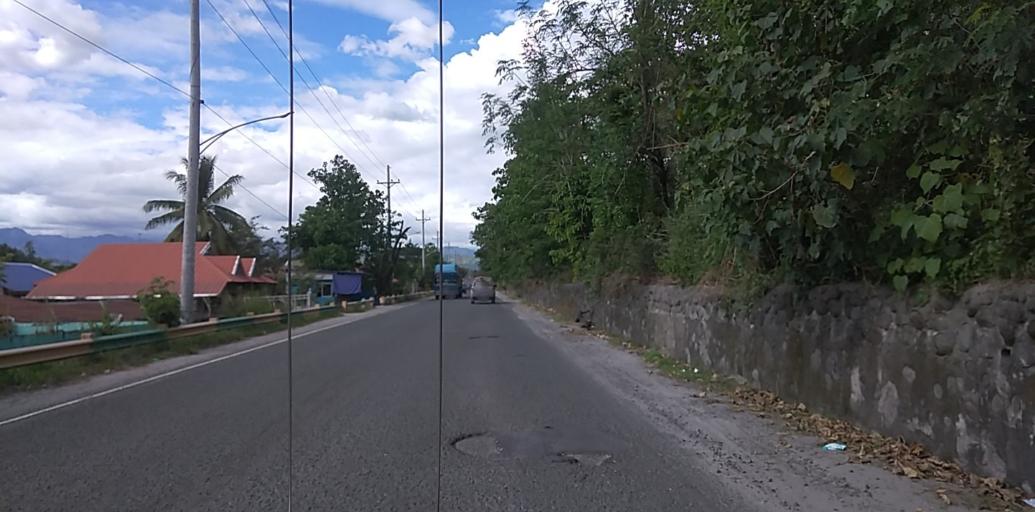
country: PH
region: Central Luzon
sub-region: Province of Pampanga
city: Dolores
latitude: 15.0932
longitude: 120.5328
